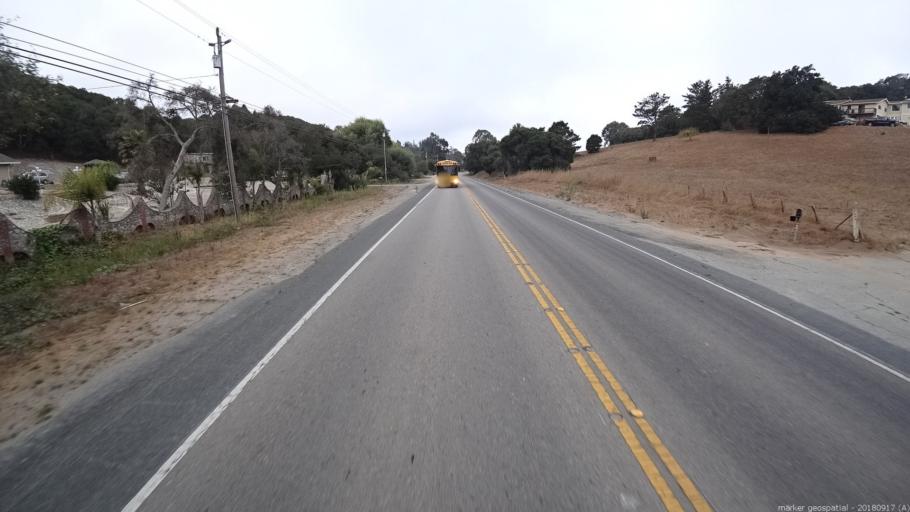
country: US
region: California
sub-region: Monterey County
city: Prunedale
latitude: 36.7988
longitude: -121.6988
